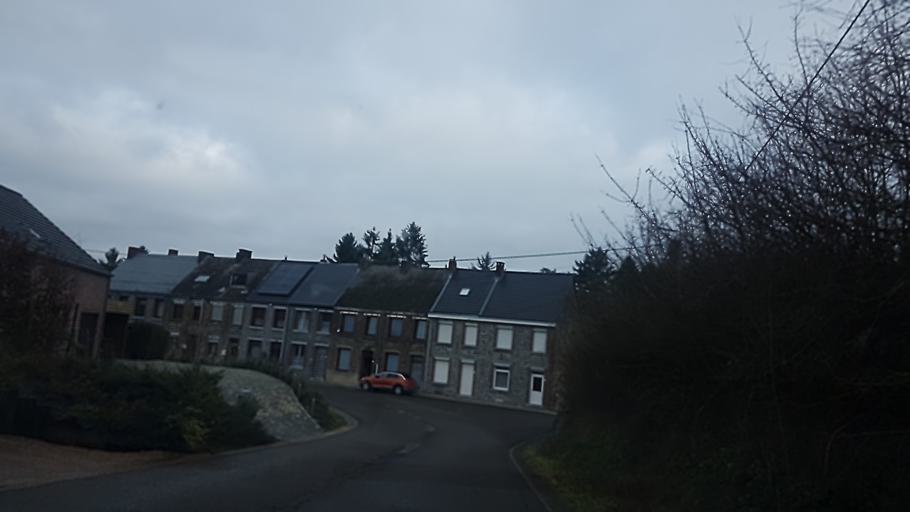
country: FR
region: Champagne-Ardenne
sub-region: Departement des Ardennes
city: Haybes
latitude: 50.0661
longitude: 4.6128
